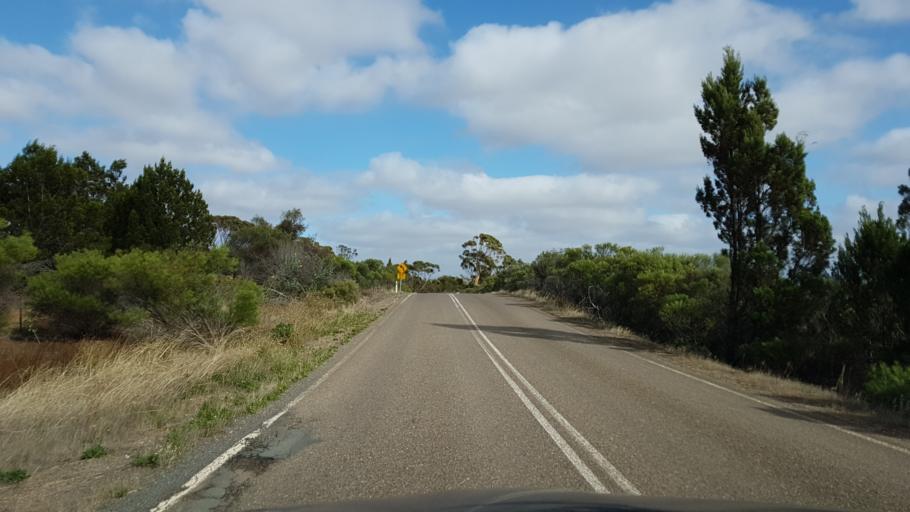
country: AU
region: South Australia
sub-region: Murray Bridge
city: Murray Bridge
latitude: -35.1128
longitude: 139.2256
